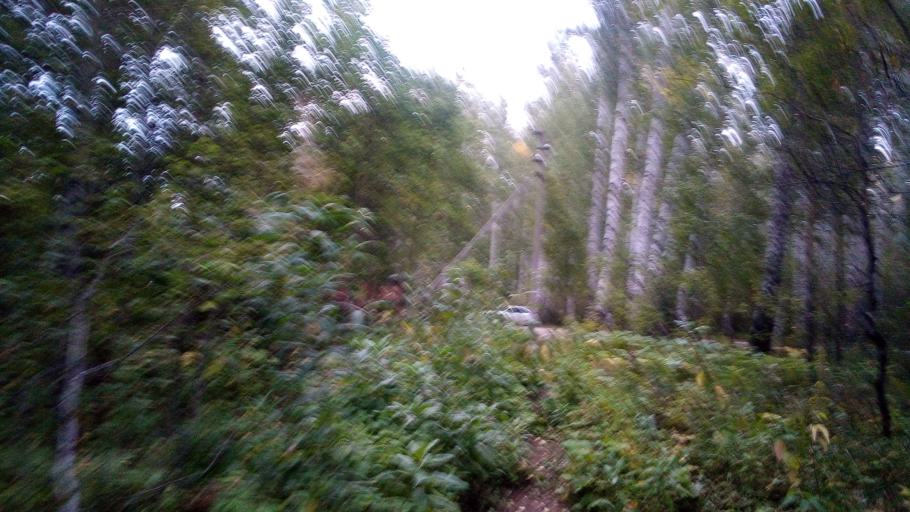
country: RU
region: Chelyabinsk
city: Tayginka
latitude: 55.4769
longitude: 60.5013
